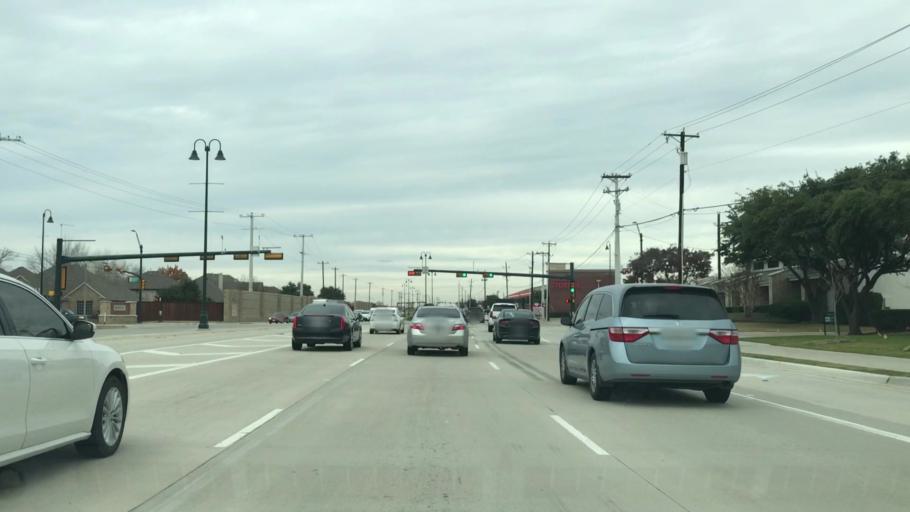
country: US
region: Texas
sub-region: Denton County
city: The Colony
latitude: 33.0731
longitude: -96.8925
